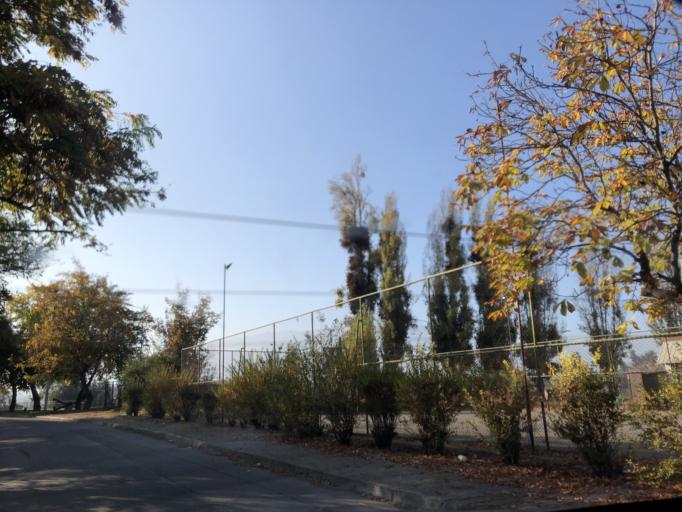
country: CL
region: Santiago Metropolitan
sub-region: Provincia de Cordillera
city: Puente Alto
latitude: -33.6261
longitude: -70.5796
